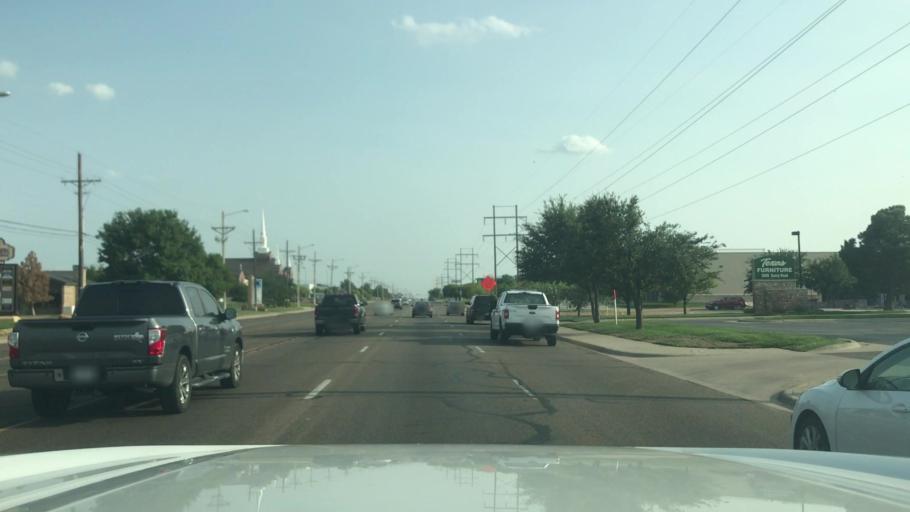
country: US
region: Texas
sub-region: Potter County
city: Amarillo
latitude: 35.1700
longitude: -101.9382
